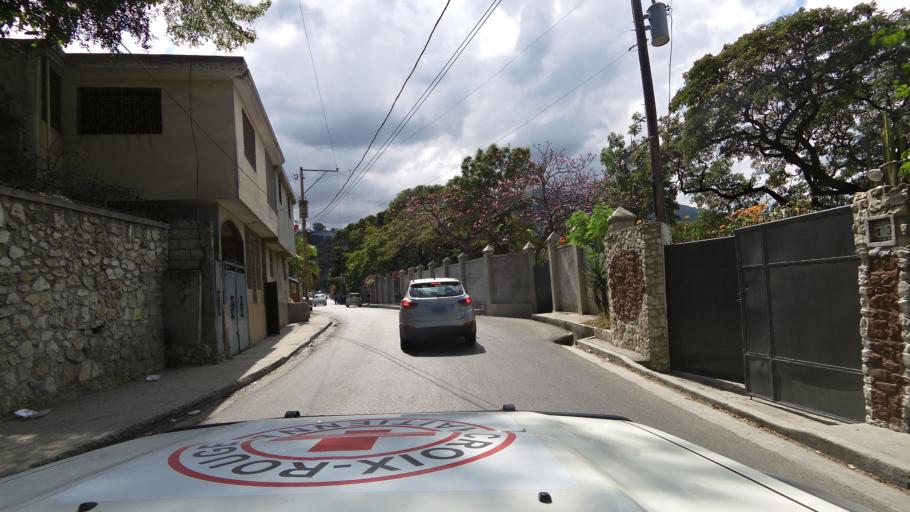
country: HT
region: Ouest
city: Delmas 73
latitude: 18.5332
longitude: -72.2967
